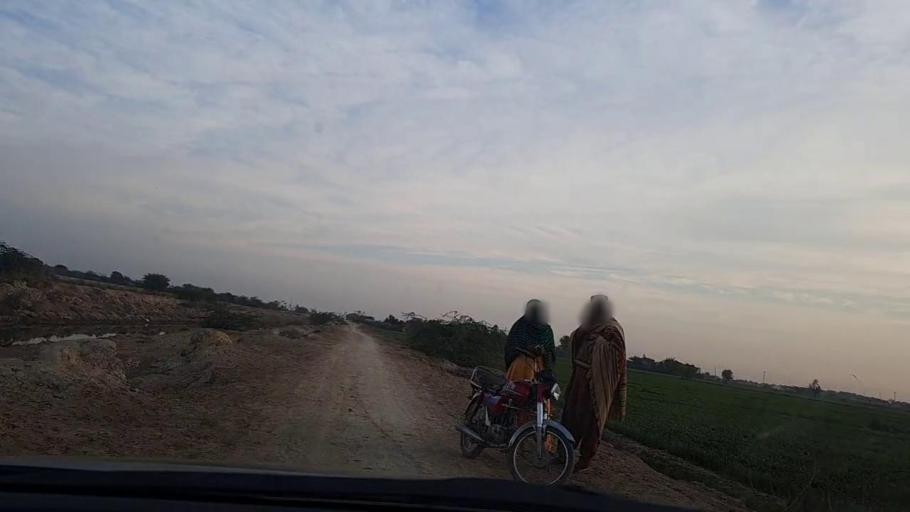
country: PK
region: Sindh
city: Sakrand
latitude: 26.1891
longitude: 68.3365
